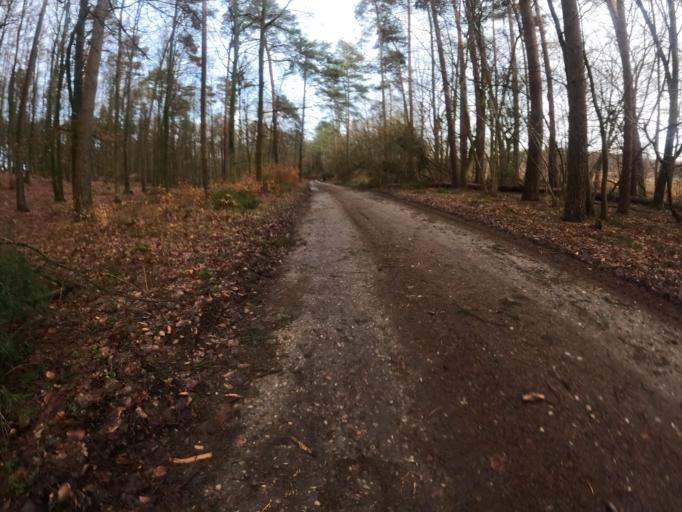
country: PL
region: West Pomeranian Voivodeship
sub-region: Powiat slawienski
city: Slawno
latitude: 54.2565
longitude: 16.6919
